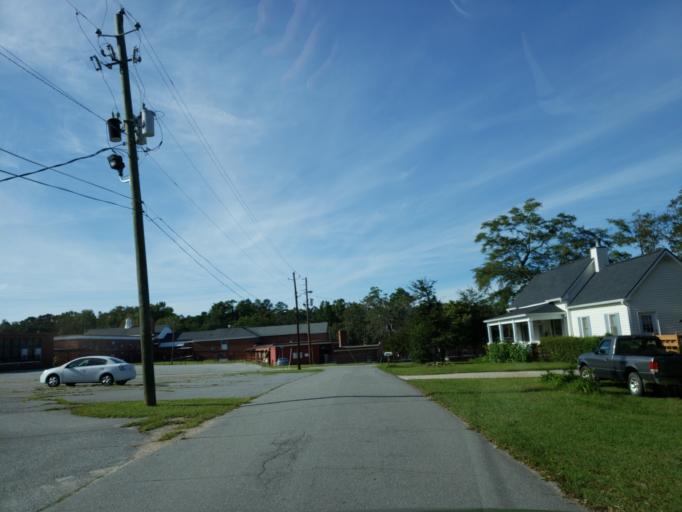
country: US
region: Georgia
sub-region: Crawford County
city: Roberta
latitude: 32.7220
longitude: -84.0087
